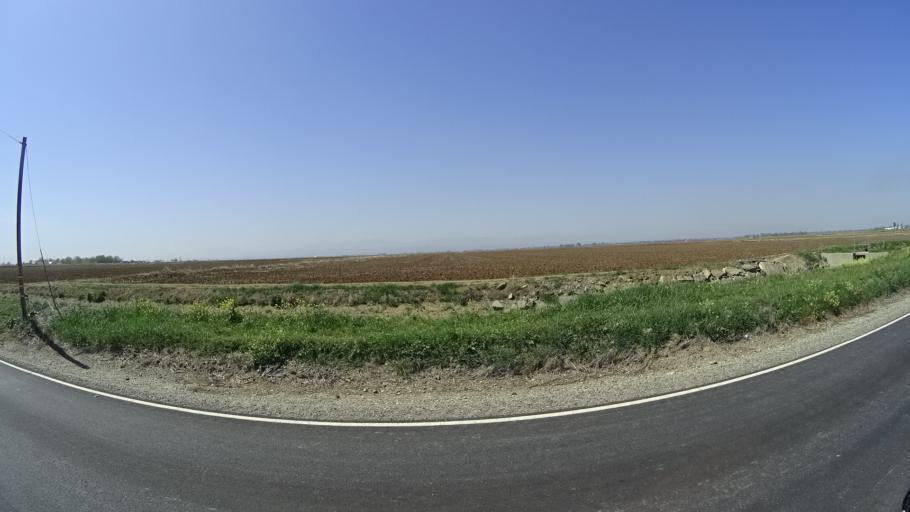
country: US
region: California
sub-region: Glenn County
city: Willows
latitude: 39.5016
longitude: -122.1367
